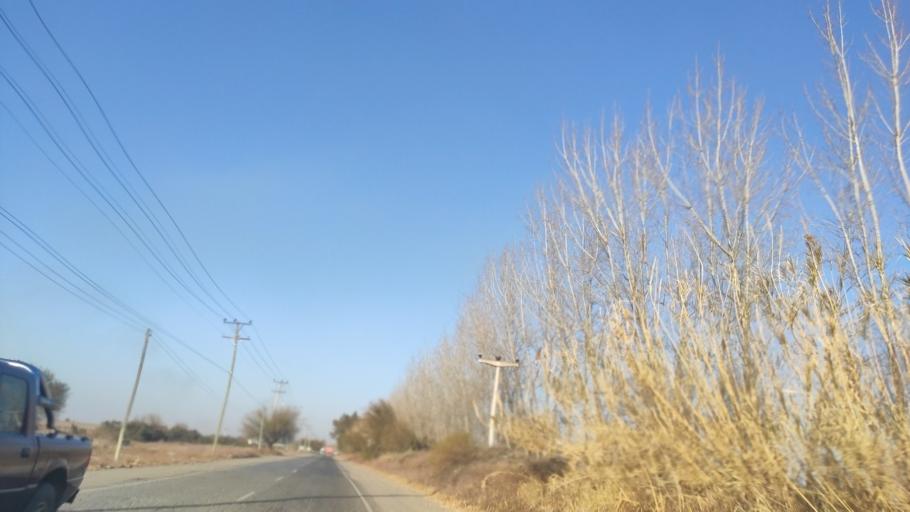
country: AR
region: San Juan
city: Villa Media Agua
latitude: -31.9793
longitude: -68.4469
